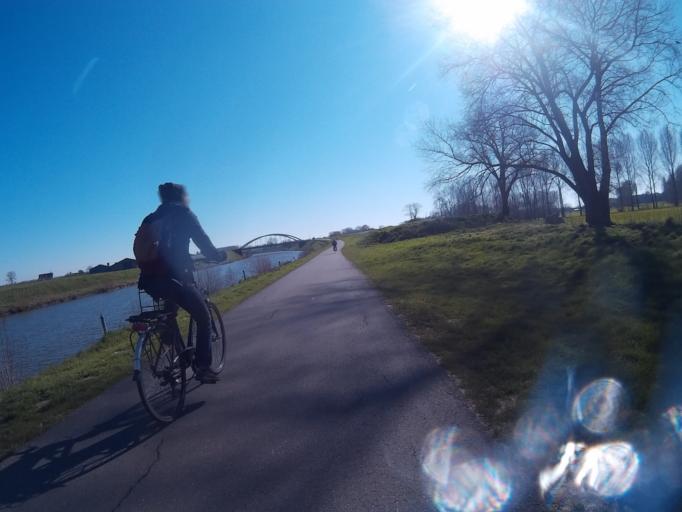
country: BE
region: Flanders
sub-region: Provincie Oost-Vlaanderen
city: Zomergem
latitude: 51.0914
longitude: 3.5200
